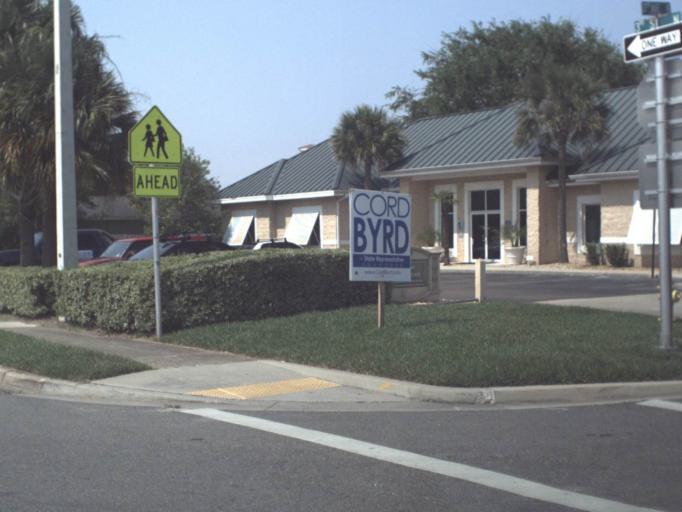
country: US
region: Florida
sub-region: Duval County
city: Neptune Beach
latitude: 30.3048
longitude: -81.3948
